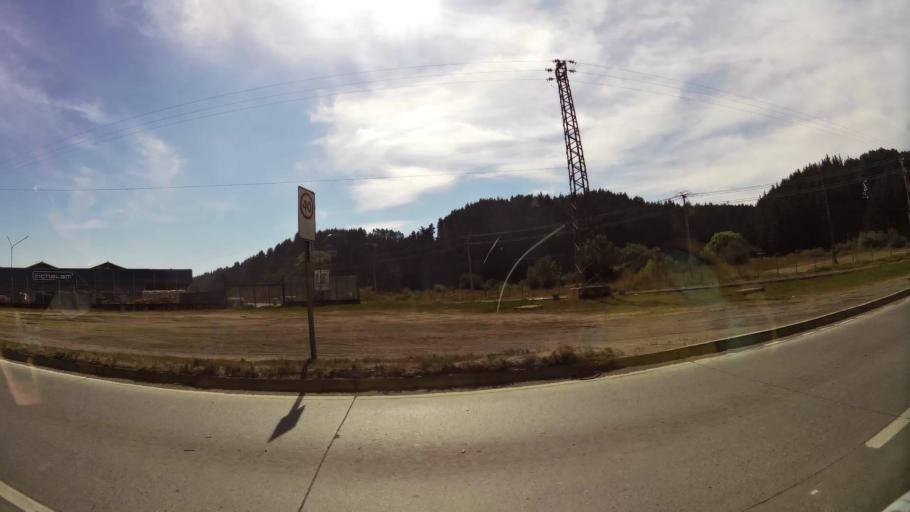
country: CL
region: Biobio
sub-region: Provincia de Concepcion
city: Talcahuano
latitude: -36.7533
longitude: -73.1238
